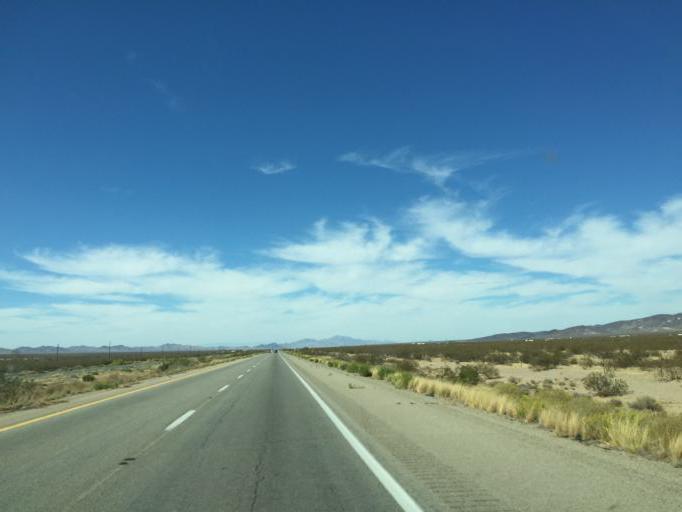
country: US
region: Arizona
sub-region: Mohave County
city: Dolan Springs
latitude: 35.5807
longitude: -114.3875
